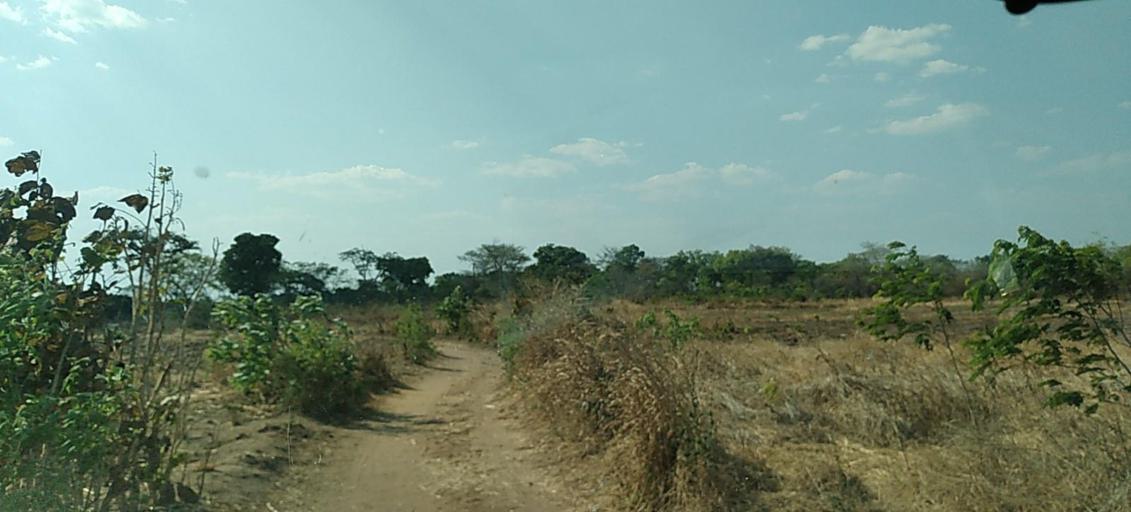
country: ZM
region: North-Western
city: Kalengwa
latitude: -13.0575
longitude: 24.9553
